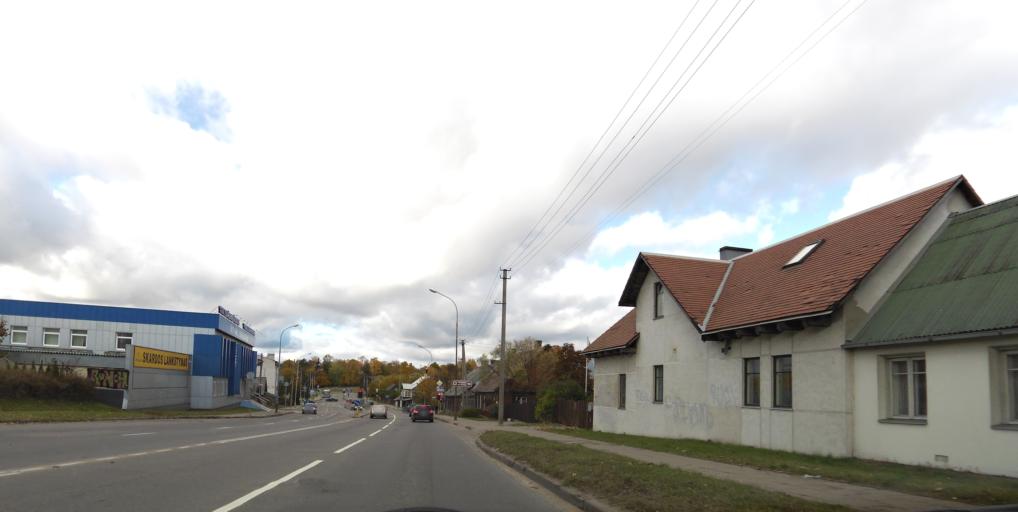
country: LT
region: Vilnius County
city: Rasos
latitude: 54.6614
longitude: 25.3026
